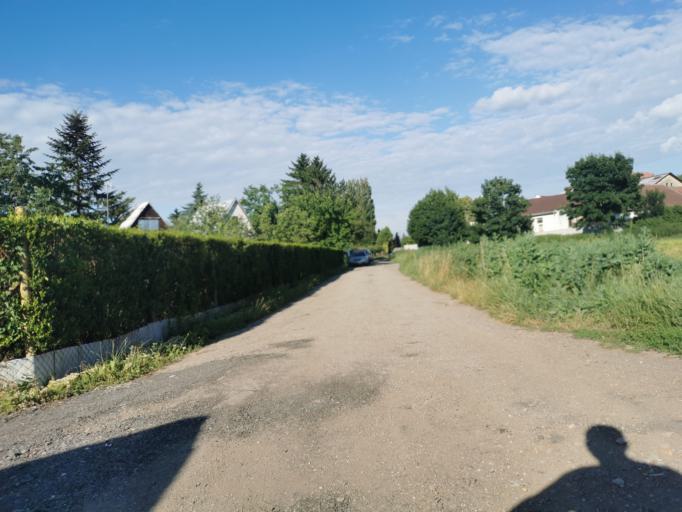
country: SK
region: Trnavsky
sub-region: Okres Skalica
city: Holic
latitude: 48.8240
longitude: 17.1525
